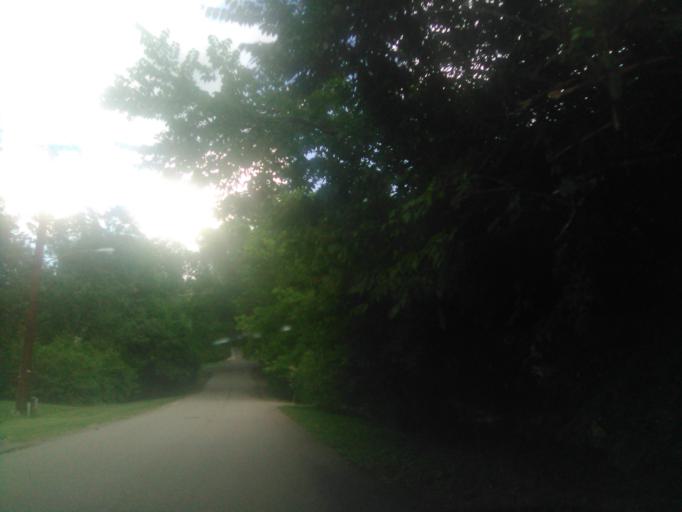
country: US
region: Tennessee
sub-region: Davidson County
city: Belle Meade
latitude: 36.0995
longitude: -86.8399
